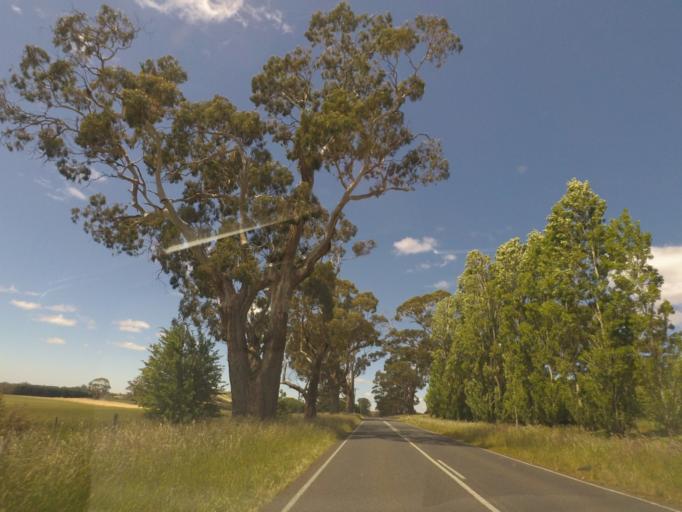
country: AU
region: Victoria
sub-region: Mount Alexander
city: Castlemaine
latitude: -37.3217
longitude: 144.2004
